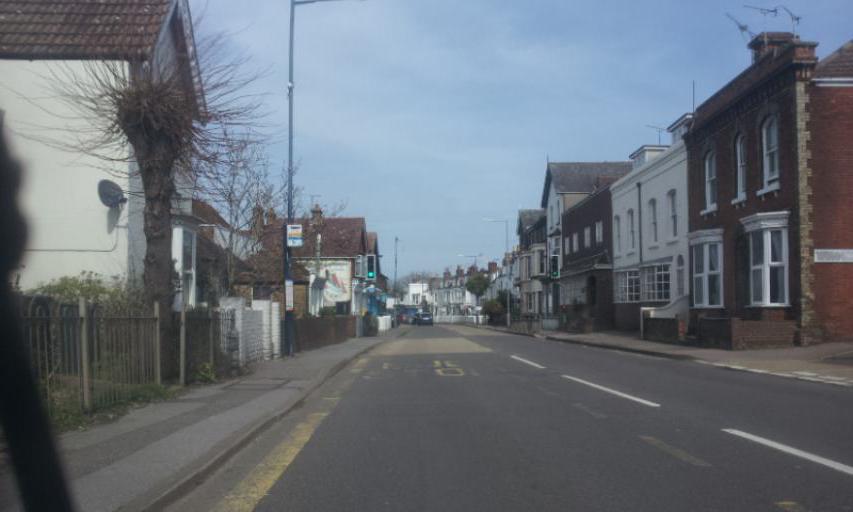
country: GB
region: England
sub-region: Kent
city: Whitstable
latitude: 51.3530
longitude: 1.0244
